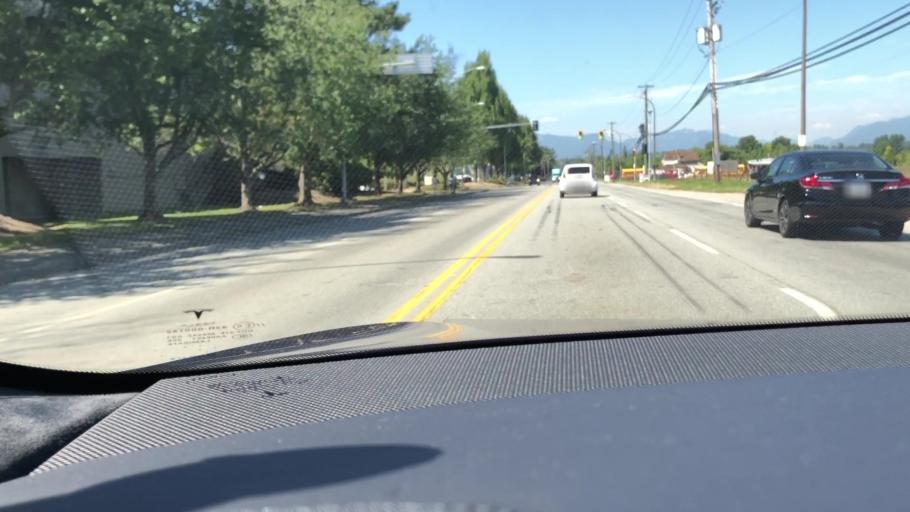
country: CA
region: British Columbia
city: Richmond
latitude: 49.1808
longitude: -123.0692
